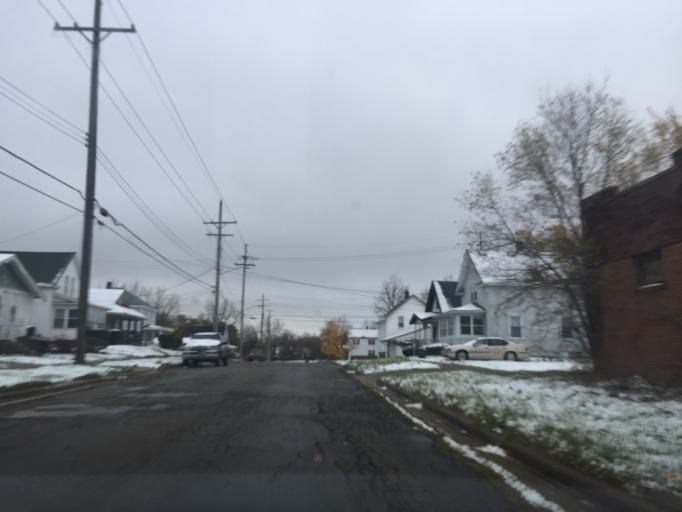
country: US
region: Michigan
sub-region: Oakland County
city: Pontiac
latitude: 42.6262
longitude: -83.2791
